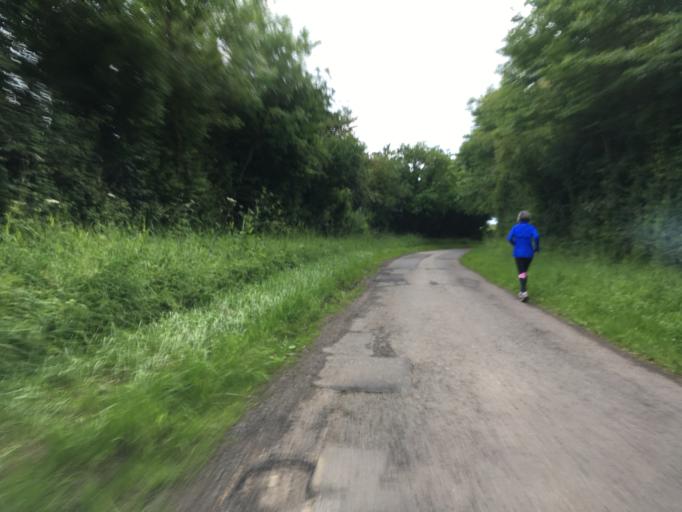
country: GB
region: England
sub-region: Gloucestershire
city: Coates
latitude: 51.6617
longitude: -2.0182
